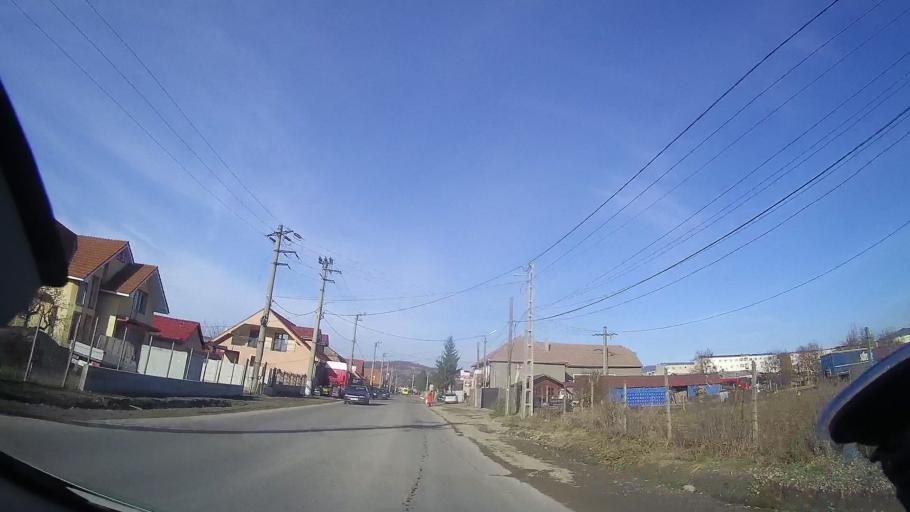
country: RO
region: Bihor
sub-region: Comuna Astileu
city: Astileu
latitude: 47.0531
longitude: 22.3920
